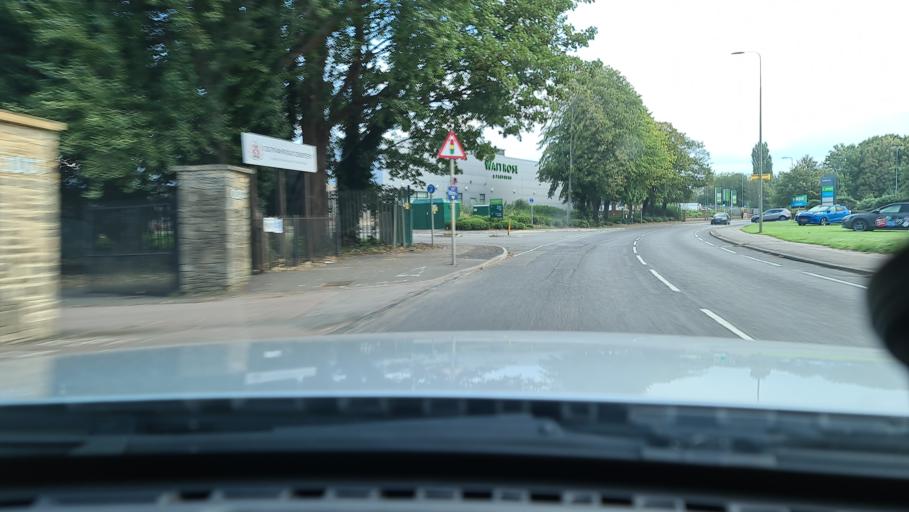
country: GB
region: England
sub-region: Oxfordshire
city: Banbury
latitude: 52.0680
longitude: -1.3405
